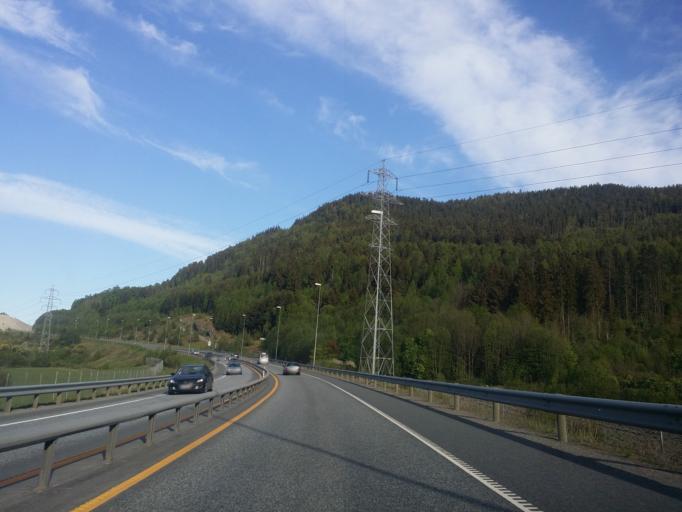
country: NO
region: Buskerud
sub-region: Nedre Eiker
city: Mjondalen
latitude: 59.7467
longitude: 10.0375
